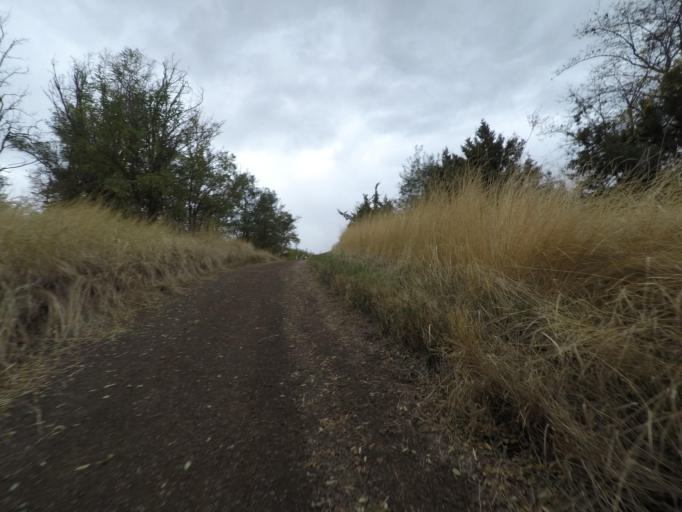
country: US
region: Washington
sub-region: Walla Walla County
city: Walla Walla East
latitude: 46.0632
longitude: -118.2563
